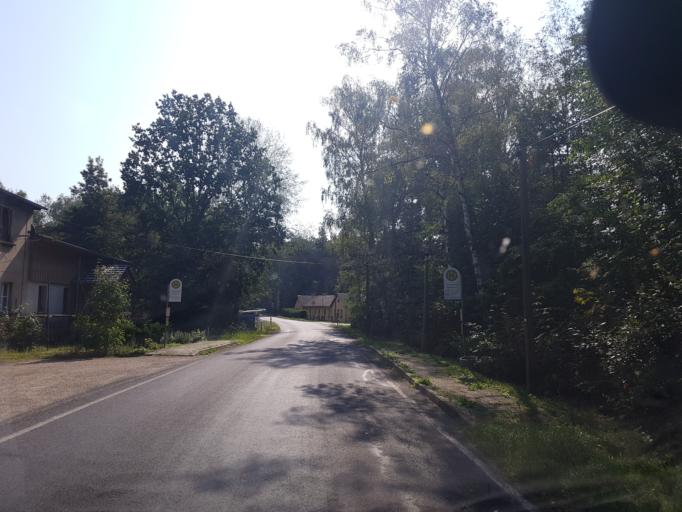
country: DE
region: Brandenburg
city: Lauchhammer
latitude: 51.5110
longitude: 13.7295
